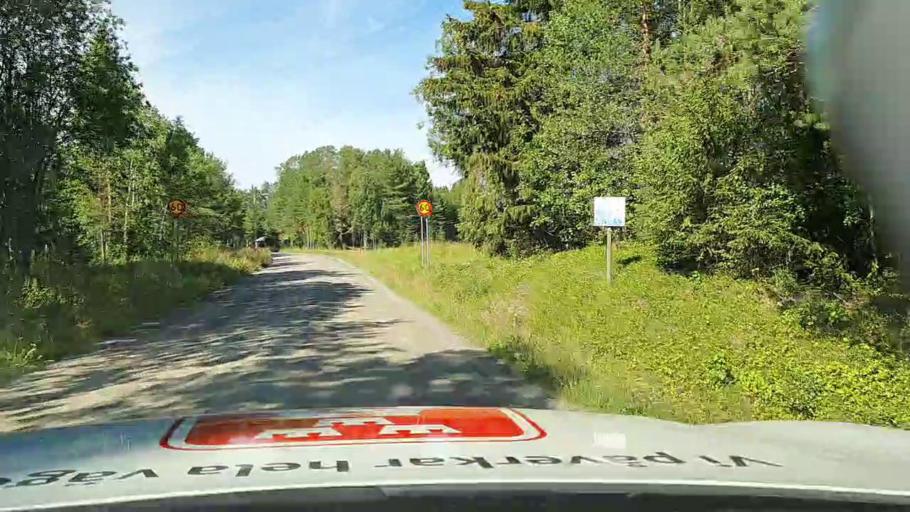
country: SE
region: Jaemtland
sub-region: Stroemsunds Kommun
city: Stroemsund
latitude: 63.6910
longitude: 15.3820
